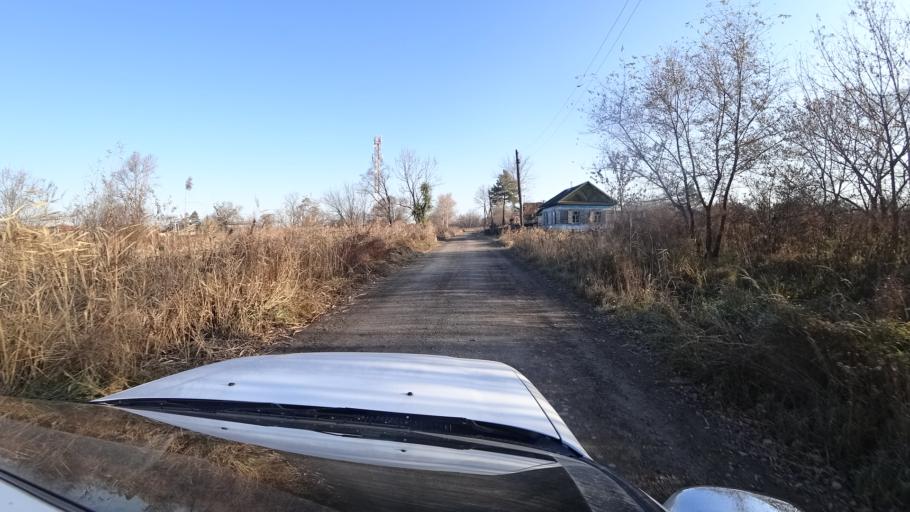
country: RU
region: Primorskiy
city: Lazo
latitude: 45.8747
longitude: 133.6465
